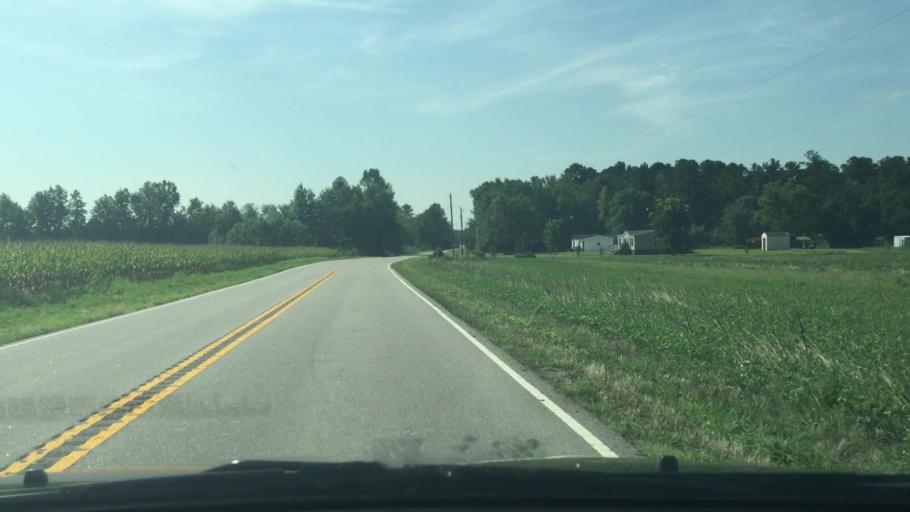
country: US
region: Virginia
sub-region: Southampton County
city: Courtland
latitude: 36.8374
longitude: -77.1292
